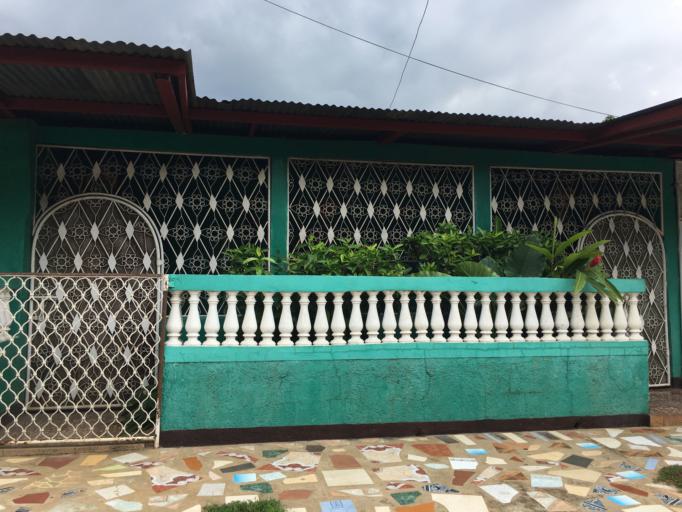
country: NI
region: Masaya
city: Masaya
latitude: 11.9823
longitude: -86.0926
